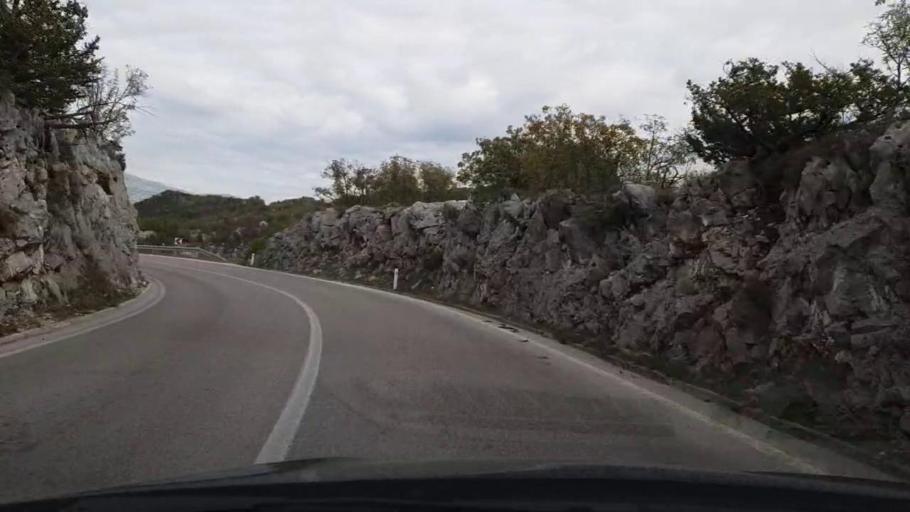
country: HR
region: Dubrovacko-Neretvanska
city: Cibaca
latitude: 42.6647
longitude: 18.2154
